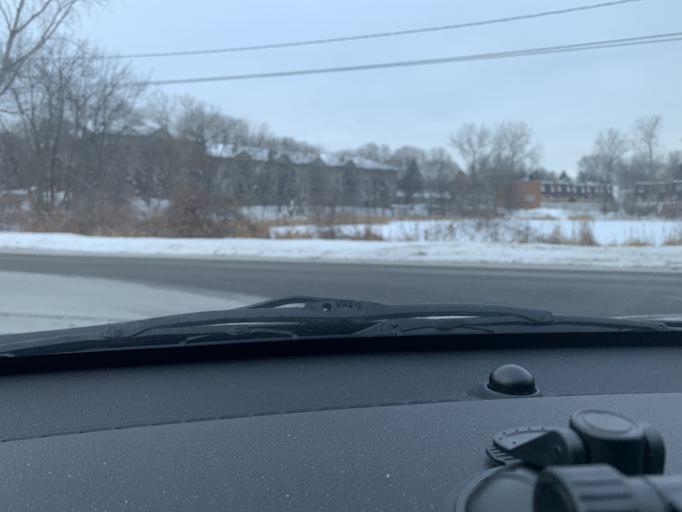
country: US
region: Minnesota
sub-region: Dakota County
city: South Saint Paul
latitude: 44.8861
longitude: -93.0602
